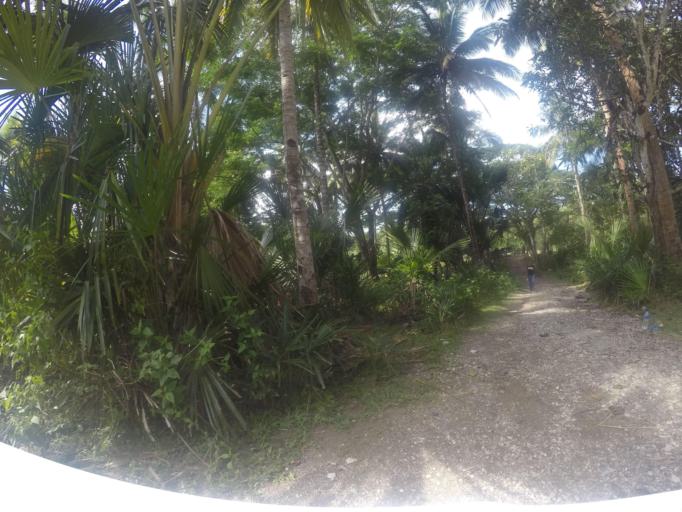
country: TL
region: Viqueque
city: Viqueque
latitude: -8.8531
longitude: 126.3559
